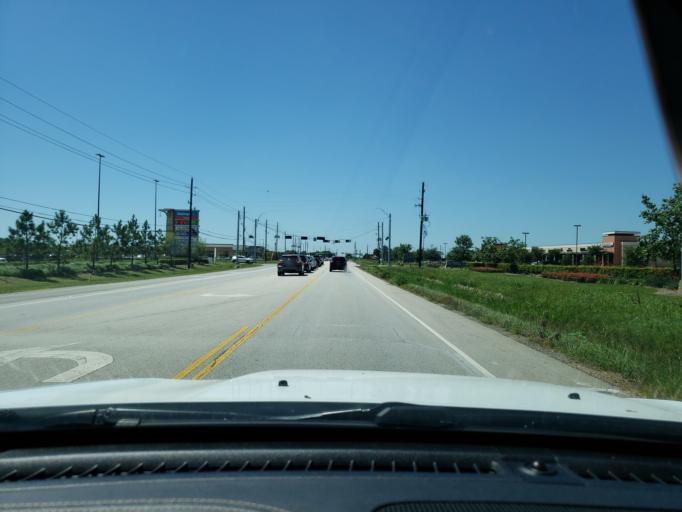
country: US
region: Texas
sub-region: Fort Bend County
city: Fulshear
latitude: 29.6991
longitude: -95.8460
